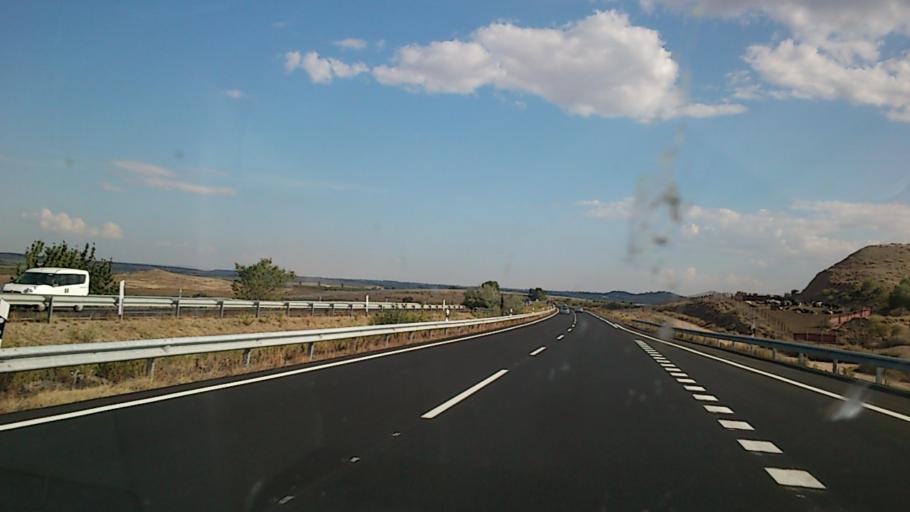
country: ES
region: Navarre
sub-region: Provincia de Navarra
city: Corella
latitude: 42.1614
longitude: -1.8223
